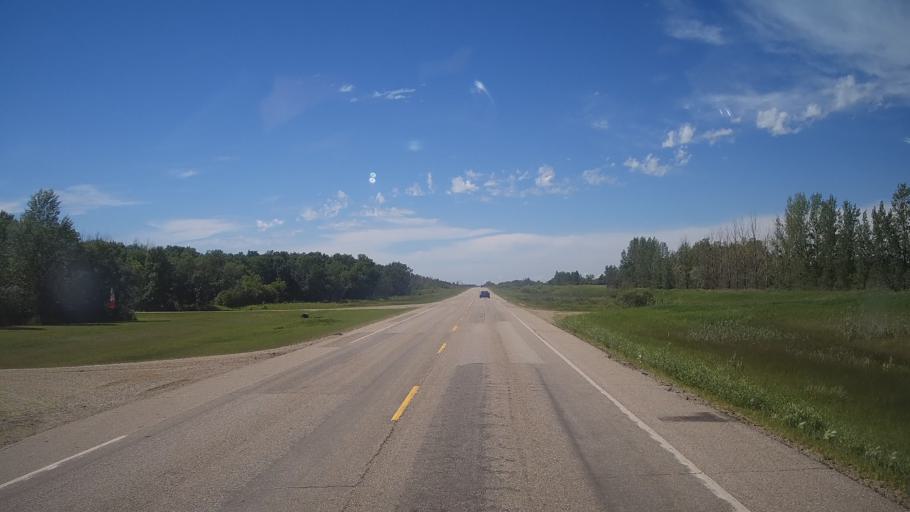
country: CA
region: Saskatchewan
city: Langenburg
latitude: 50.7956
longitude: -101.5628
